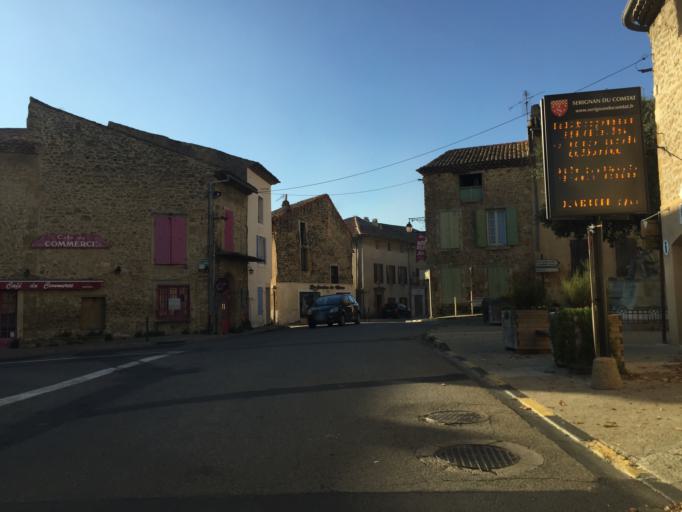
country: FR
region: Provence-Alpes-Cote d'Azur
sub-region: Departement du Vaucluse
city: Serignan-du-Comtat
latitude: 44.1887
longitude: 4.8449
